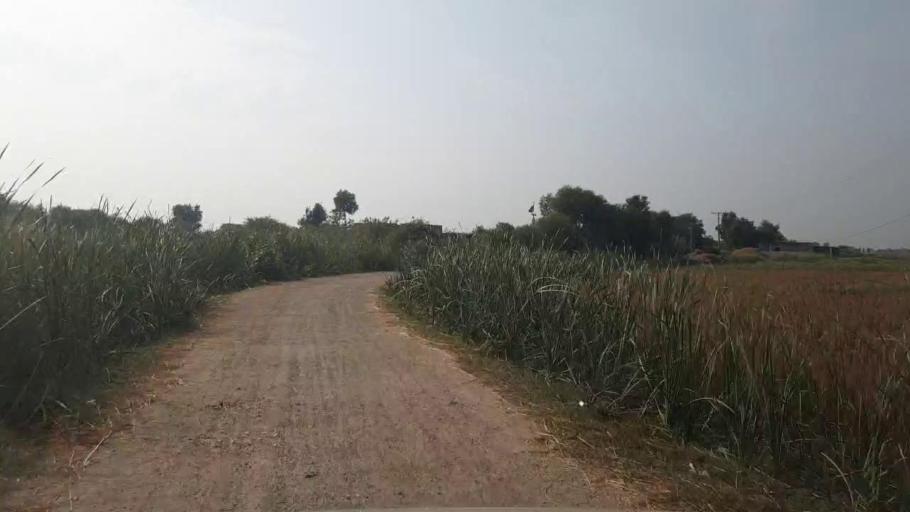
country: PK
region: Sindh
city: Tando Muhammad Khan
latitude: 25.1100
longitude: 68.4951
